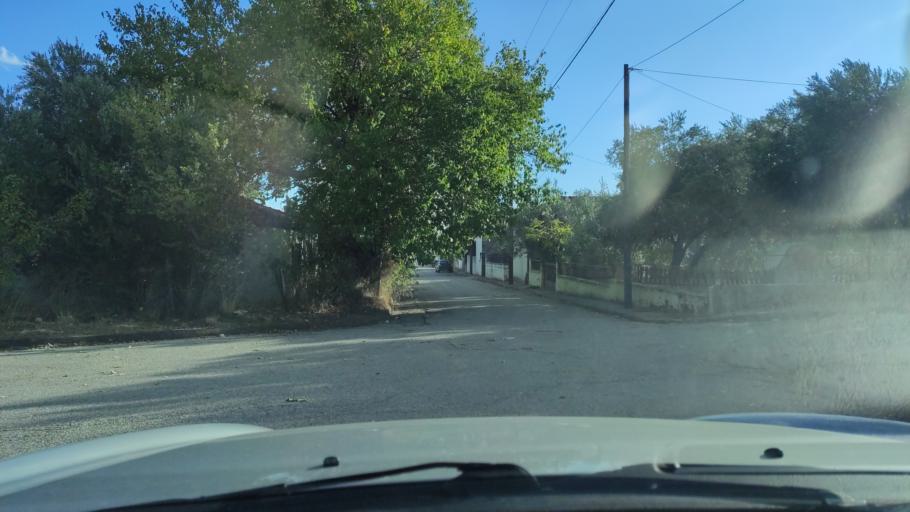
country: GR
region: East Macedonia and Thrace
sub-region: Nomos Xanthis
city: Selero
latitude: 41.1243
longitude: 25.0640
